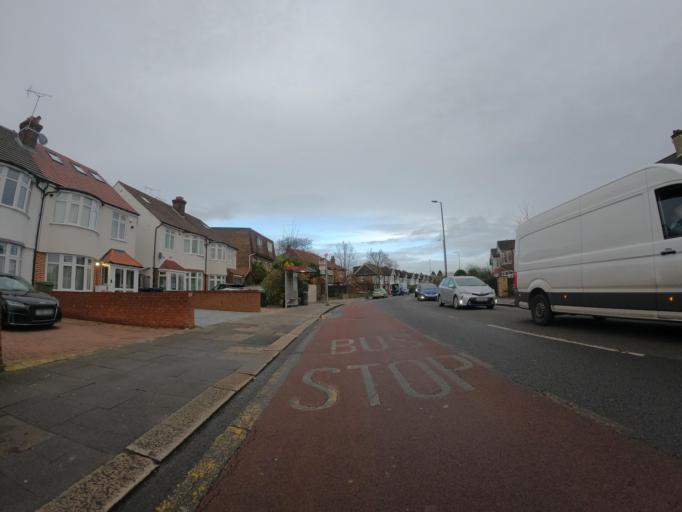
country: GB
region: England
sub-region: Greater London
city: Ealing
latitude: 51.5016
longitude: -0.2943
